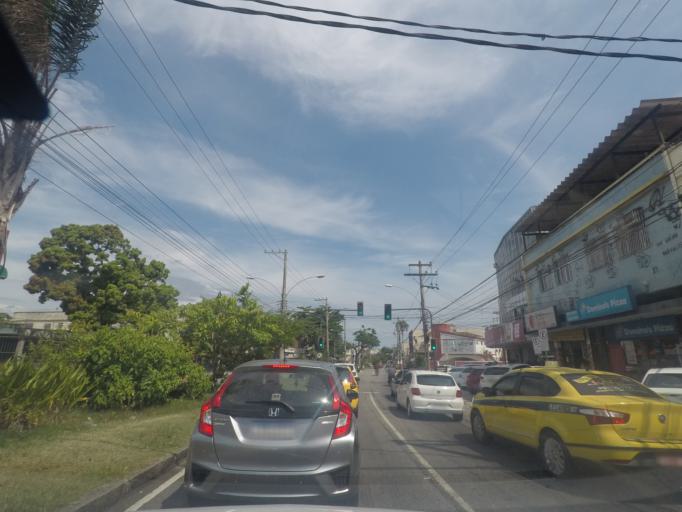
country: BR
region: Rio de Janeiro
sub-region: Rio De Janeiro
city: Rio de Janeiro
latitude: -22.8069
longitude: -43.1979
